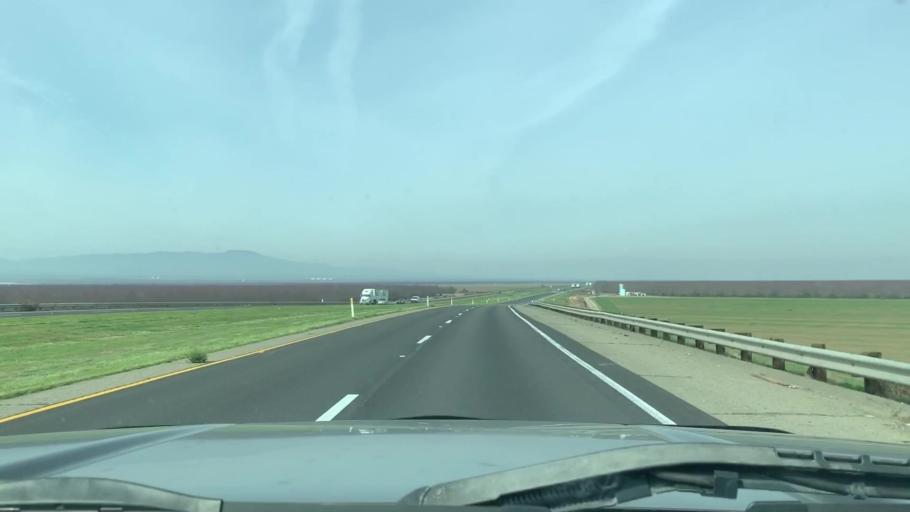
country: US
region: California
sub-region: Fresno County
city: Huron
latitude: 36.1774
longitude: -120.1949
